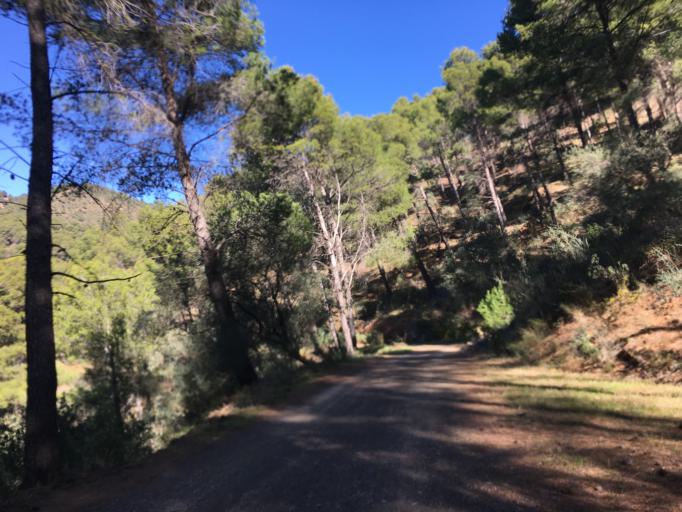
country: ES
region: Andalusia
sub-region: Provincia de Malaga
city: Malaga
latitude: 36.8017
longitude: -4.3993
